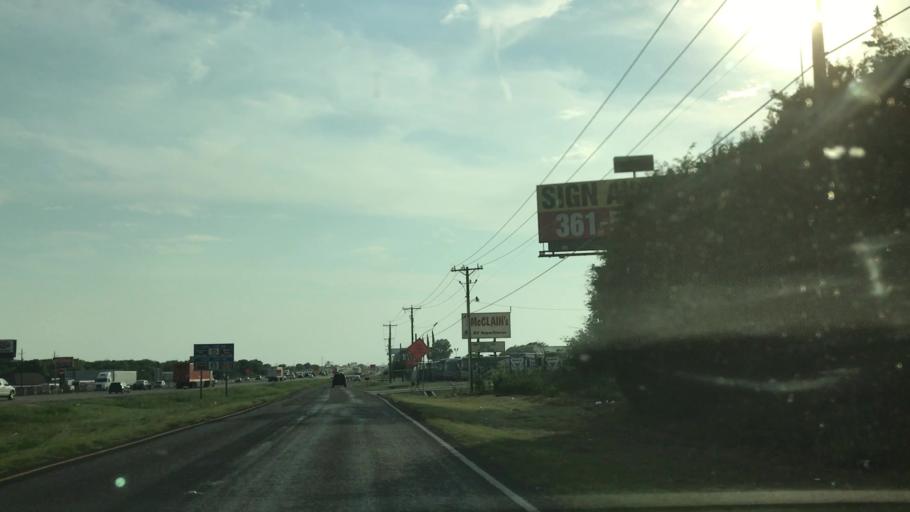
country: US
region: Texas
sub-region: Rockwall County
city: Fate
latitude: 32.9241
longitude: -96.4019
